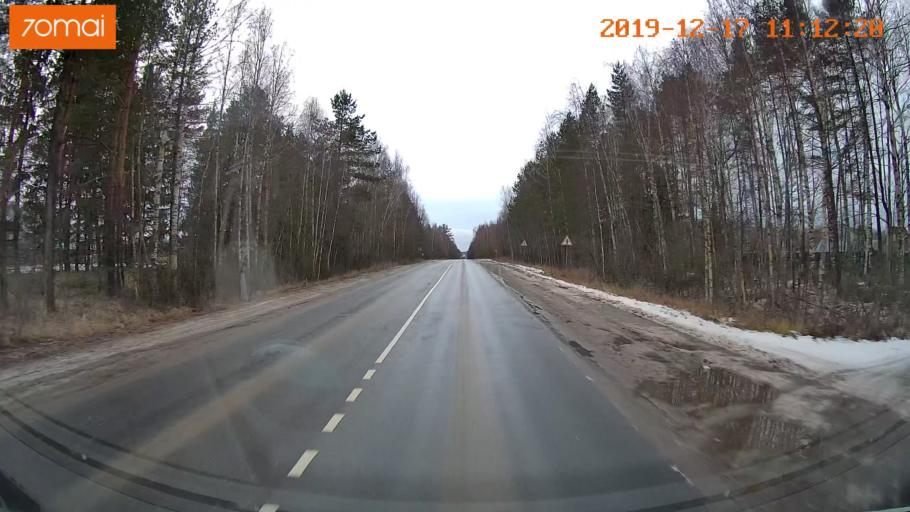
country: RU
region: Vladimir
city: Gus'-Khrustal'nyy
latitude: 55.5771
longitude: 40.6295
